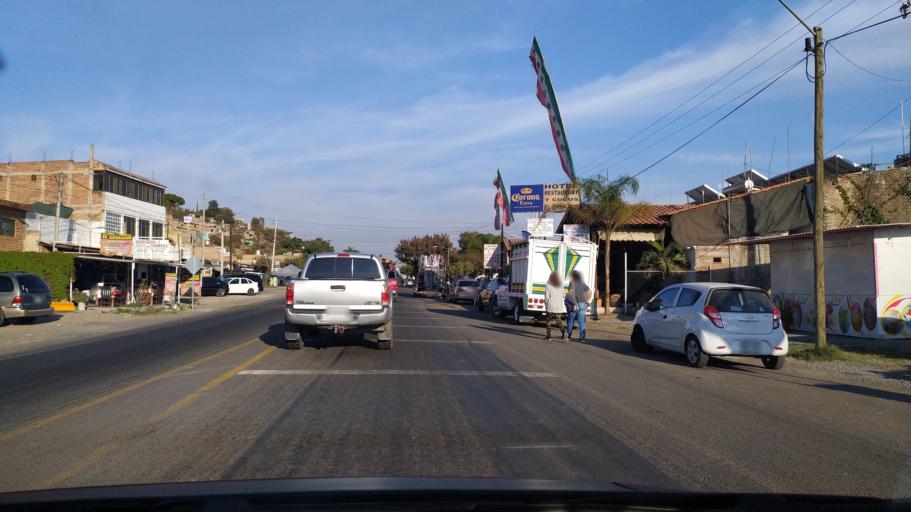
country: MX
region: Jalisco
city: Jamay
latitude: 20.2928
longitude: -102.7176
